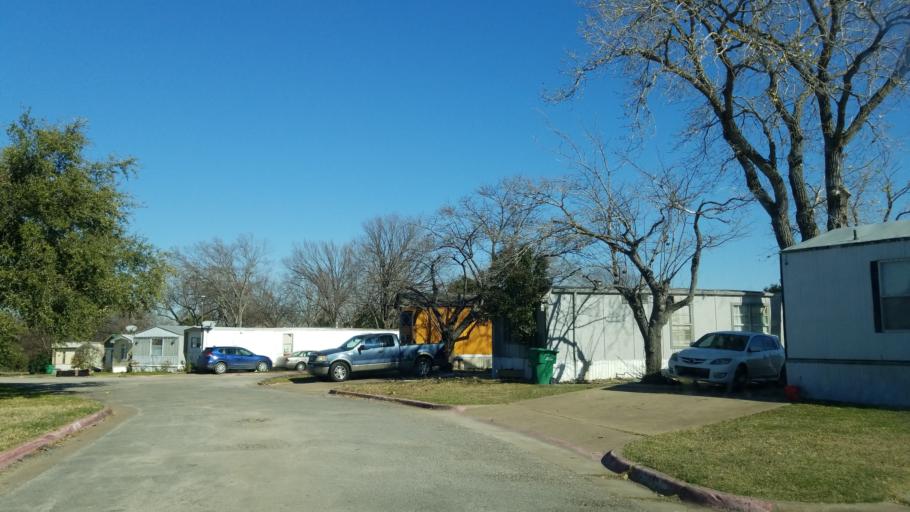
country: US
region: Texas
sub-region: Dallas County
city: Cockrell Hill
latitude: 32.7589
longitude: -96.9127
